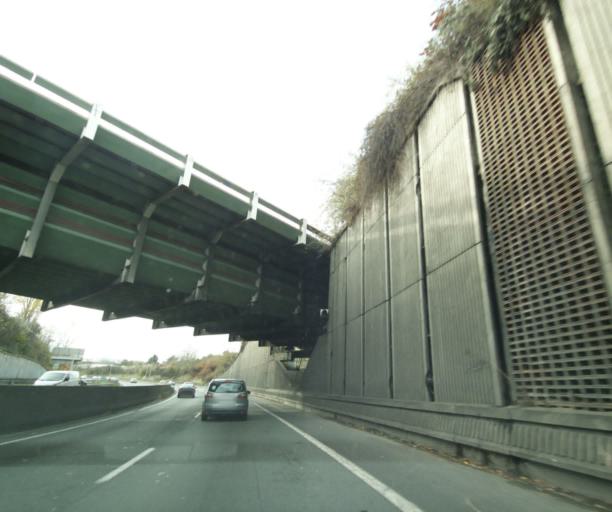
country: FR
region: Midi-Pyrenees
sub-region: Departement de la Haute-Garonne
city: Ramonville-Saint-Agne
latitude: 43.5744
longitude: 1.4695
